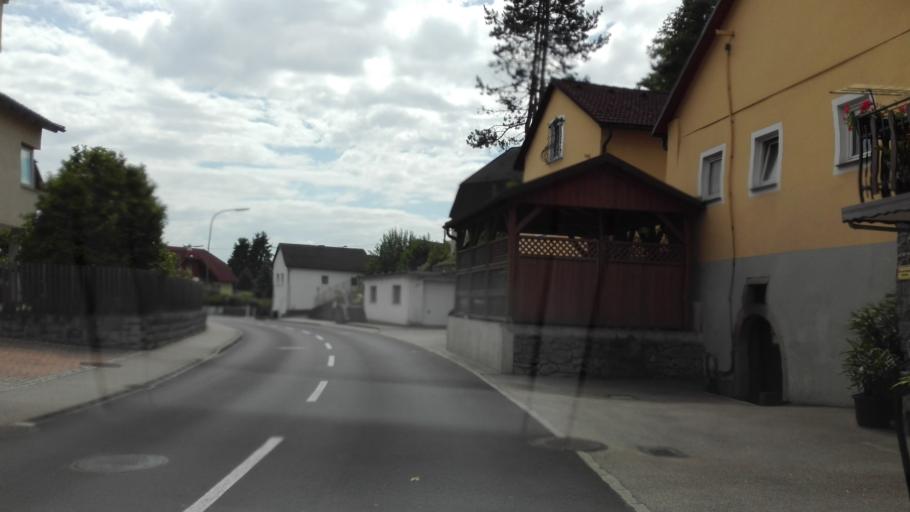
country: AT
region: Upper Austria
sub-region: Politischer Bezirk Perg
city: Perg
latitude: 48.2519
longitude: 14.6324
